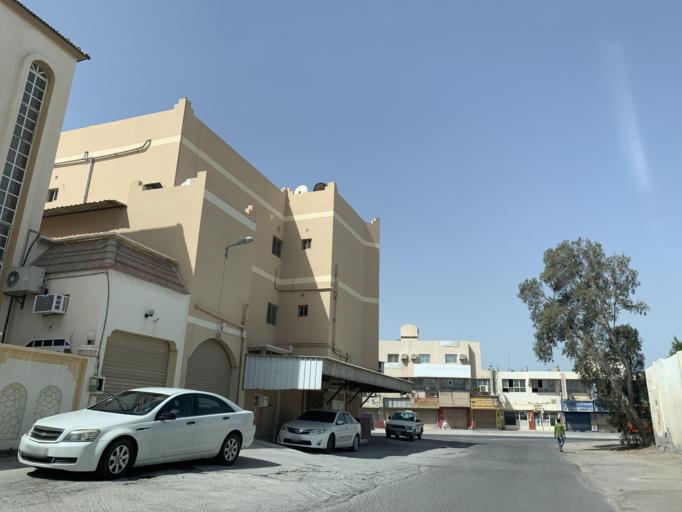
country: BH
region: Northern
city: Sitrah
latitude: 26.1422
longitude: 50.6037
